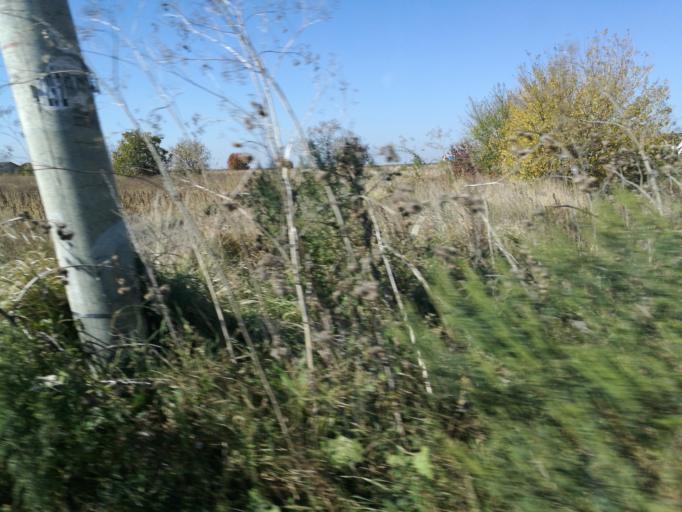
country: RO
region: Giurgiu
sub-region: Comuna Joita
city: Bacu
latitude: 44.4716
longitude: 25.8867
